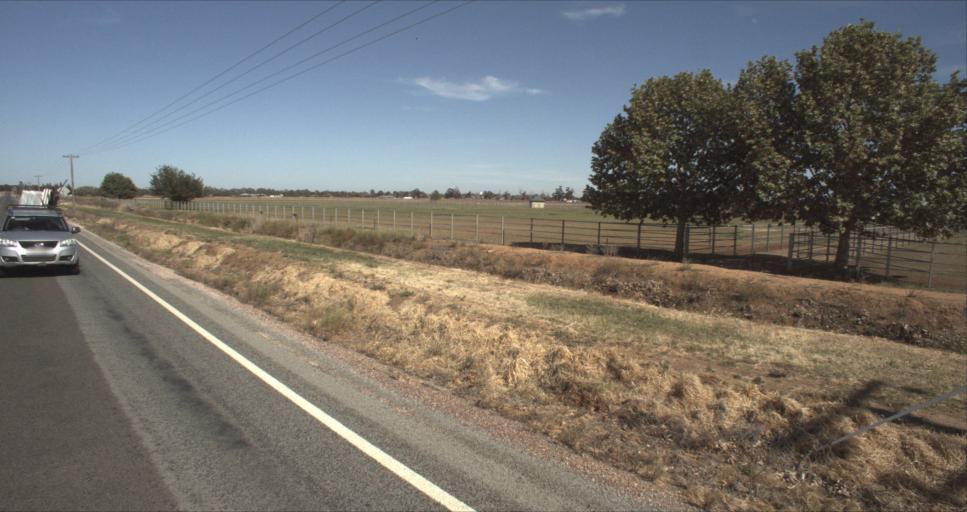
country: AU
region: New South Wales
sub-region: Leeton
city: Leeton
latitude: -34.5596
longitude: 146.4402
